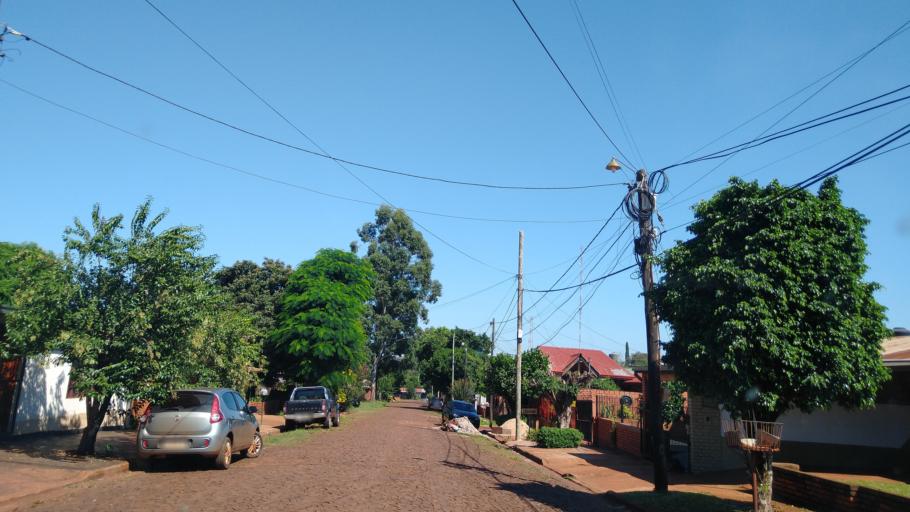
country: AR
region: Misiones
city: Puerto Libertad
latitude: -25.9674
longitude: -54.5609
